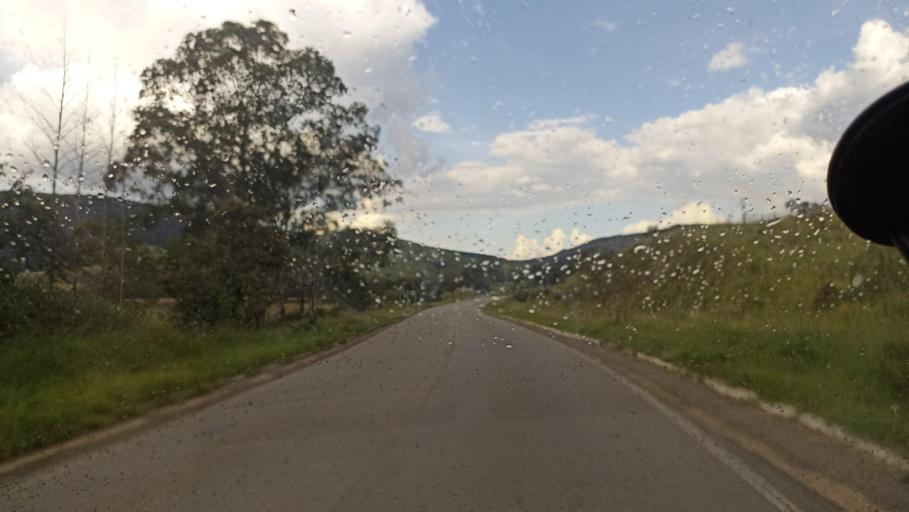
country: BR
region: Minas Gerais
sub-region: Baependi
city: Baependi
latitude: -21.9218
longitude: -44.8247
